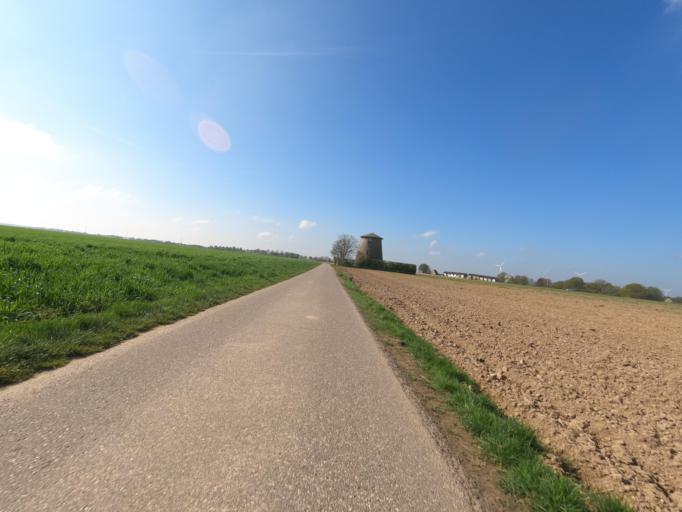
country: DE
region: North Rhine-Westphalia
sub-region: Regierungsbezirk Koln
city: Heinsberg
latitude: 51.0425
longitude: 6.0788
